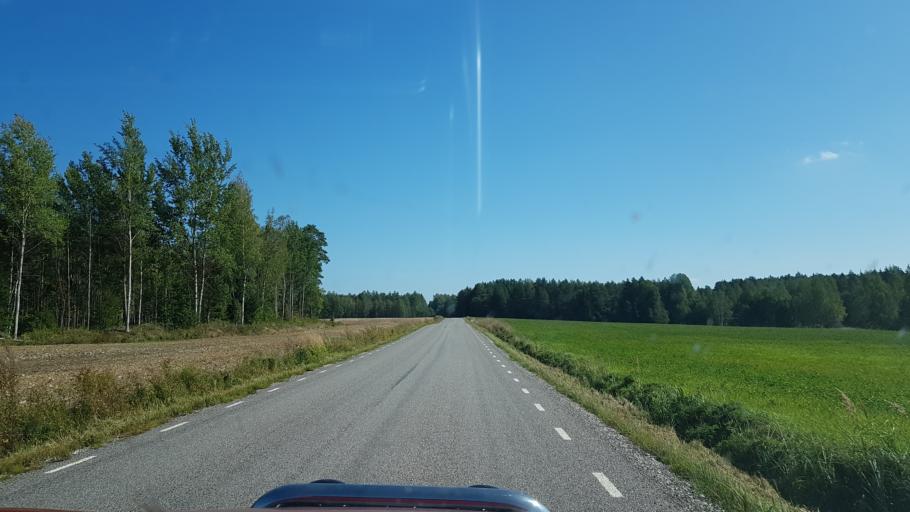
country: EE
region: Polvamaa
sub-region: Polva linn
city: Polva
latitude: 58.2093
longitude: 27.1218
